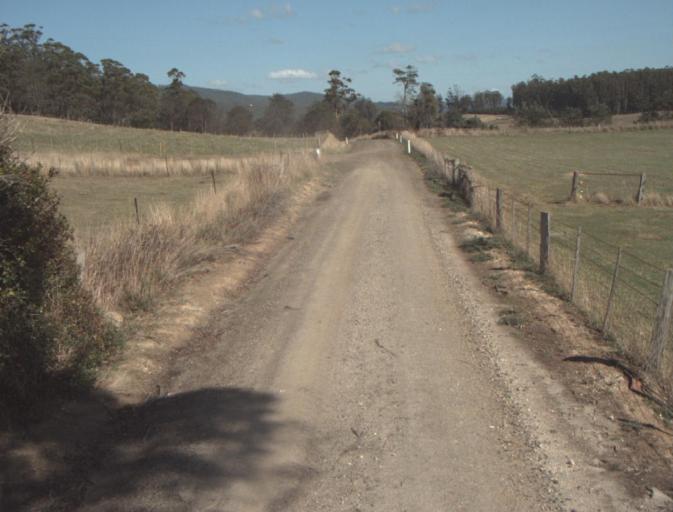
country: AU
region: Tasmania
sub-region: Launceston
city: Mayfield
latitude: -41.2212
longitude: 147.2390
